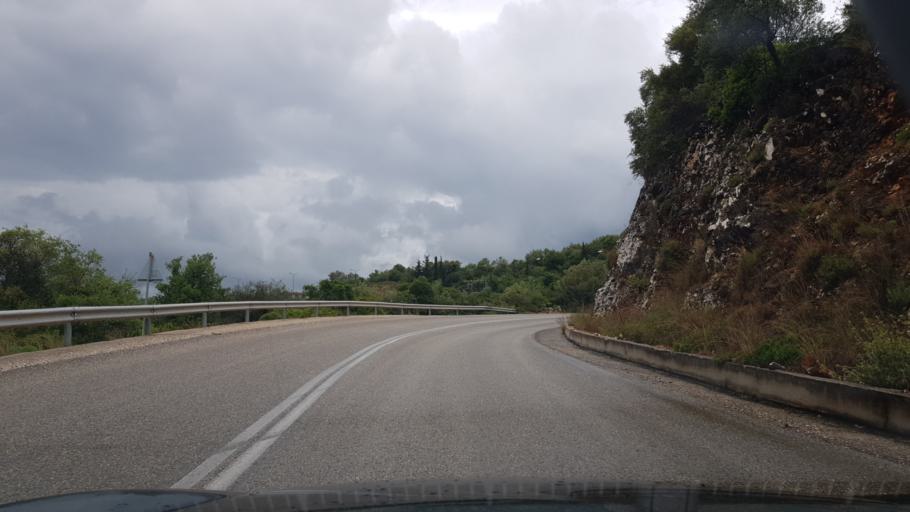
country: GR
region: Ionian Islands
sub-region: Lefkada
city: Nidri
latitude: 38.6513
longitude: 20.6833
